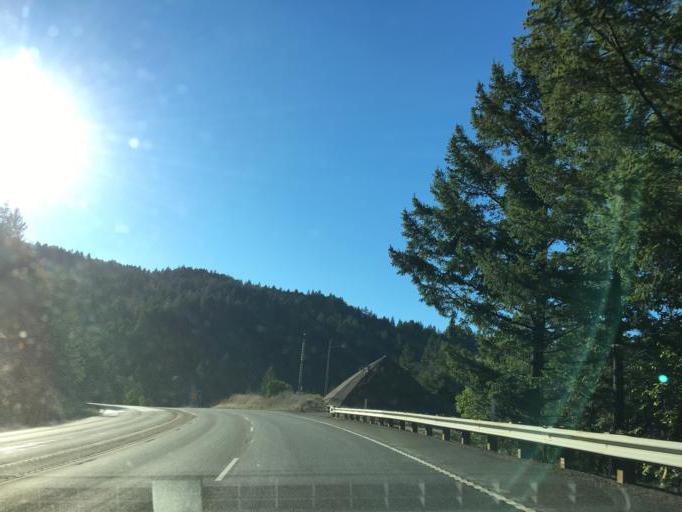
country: US
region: California
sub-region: Mendocino County
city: Laytonville
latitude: 39.8278
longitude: -123.5896
